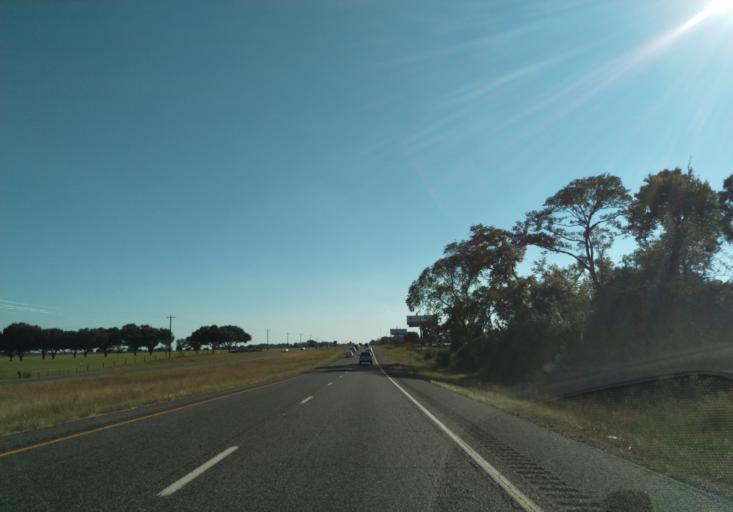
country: US
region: Texas
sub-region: Waller County
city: Hempstead
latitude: 30.1550
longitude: -96.0688
